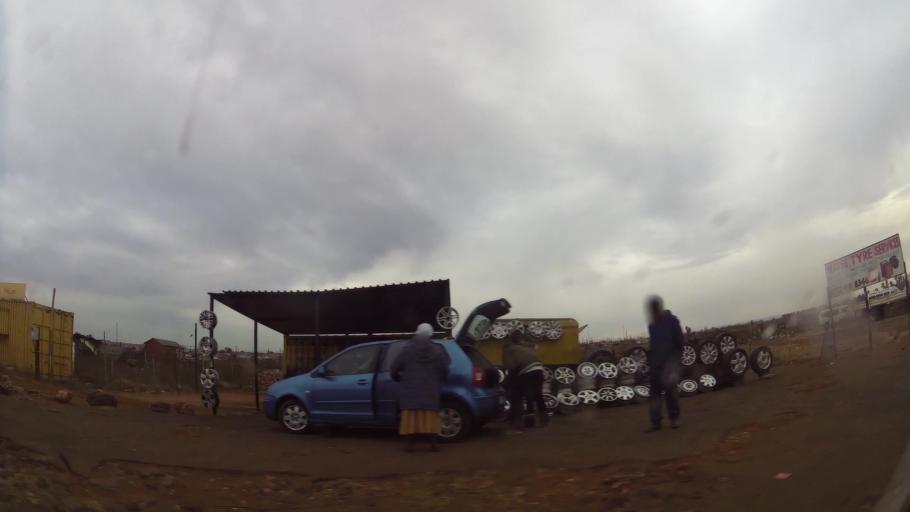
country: ZA
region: Gauteng
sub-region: Ekurhuleni Metropolitan Municipality
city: Germiston
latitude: -26.3762
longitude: 28.1732
